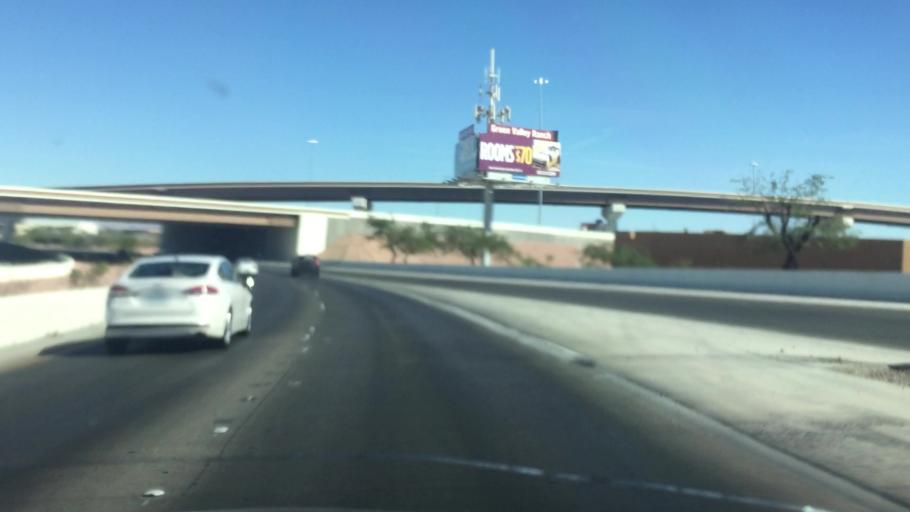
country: US
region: Nevada
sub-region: Clark County
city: Paradise
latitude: 36.0616
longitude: -115.1507
